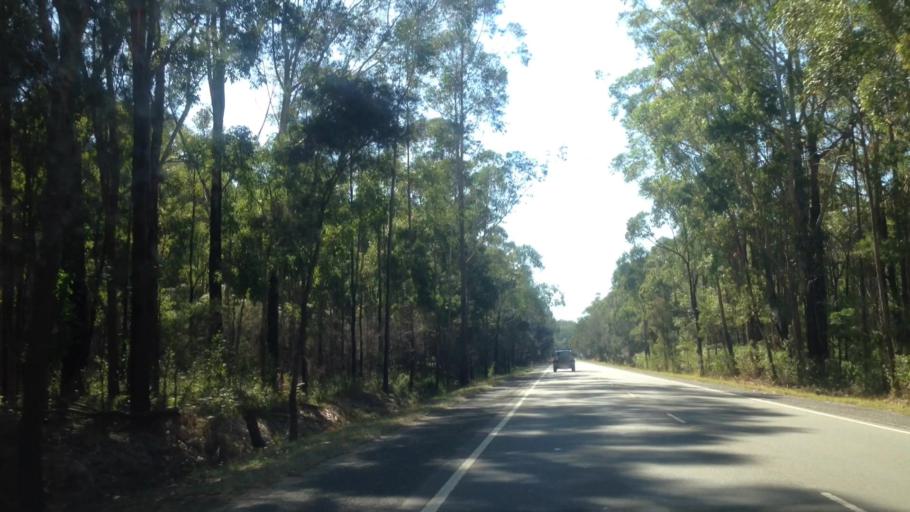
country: AU
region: New South Wales
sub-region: Lake Macquarie Shire
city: Toronto
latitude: -32.9871
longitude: 151.5093
